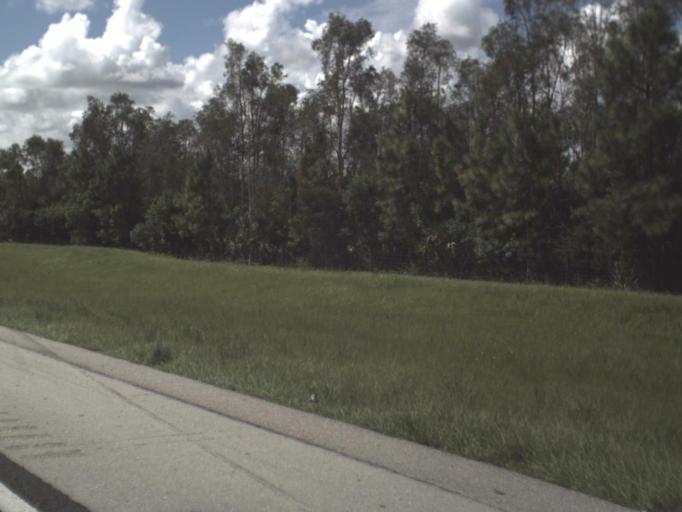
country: US
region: Florida
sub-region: Lee County
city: Estero
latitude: 26.4469
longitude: -81.7834
